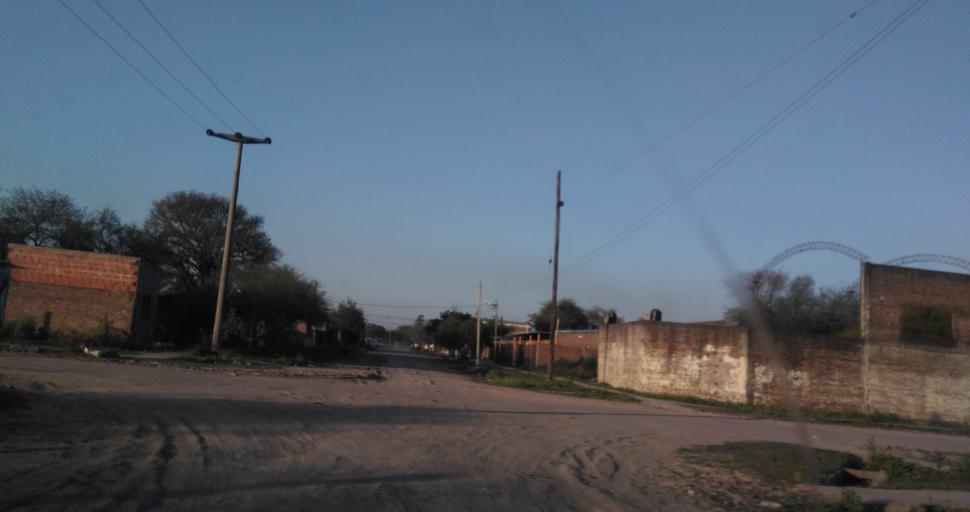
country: AR
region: Chaco
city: Resistencia
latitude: -27.4744
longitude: -59.0089
